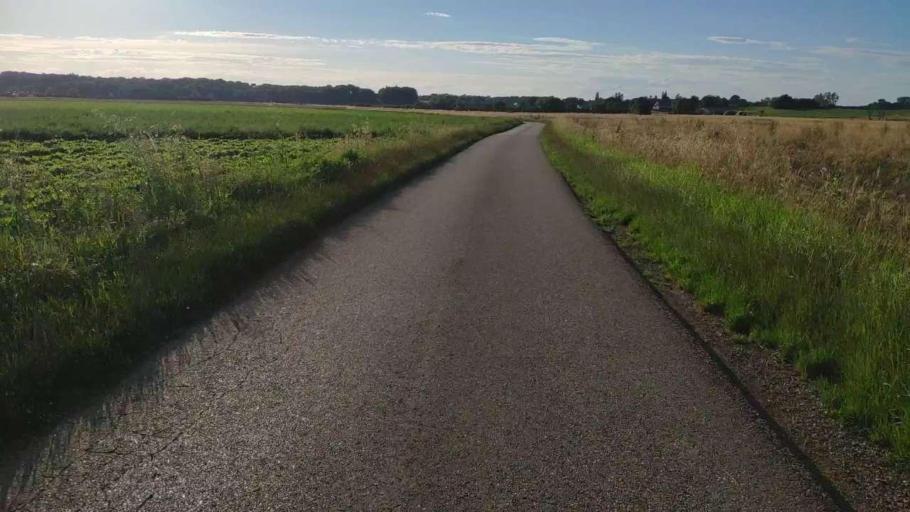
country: FR
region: Franche-Comte
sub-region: Departement du Jura
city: Bletterans
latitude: 46.7715
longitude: 5.4997
